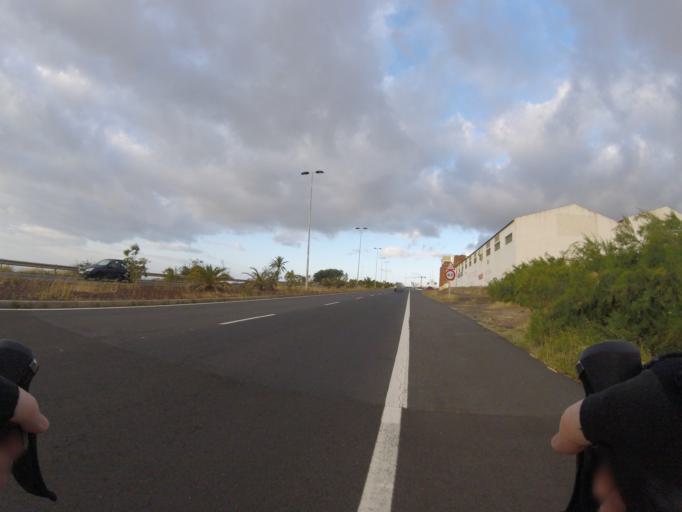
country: ES
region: Canary Islands
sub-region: Provincia de Santa Cruz de Tenerife
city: La Laguna
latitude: 28.4295
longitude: -16.3122
